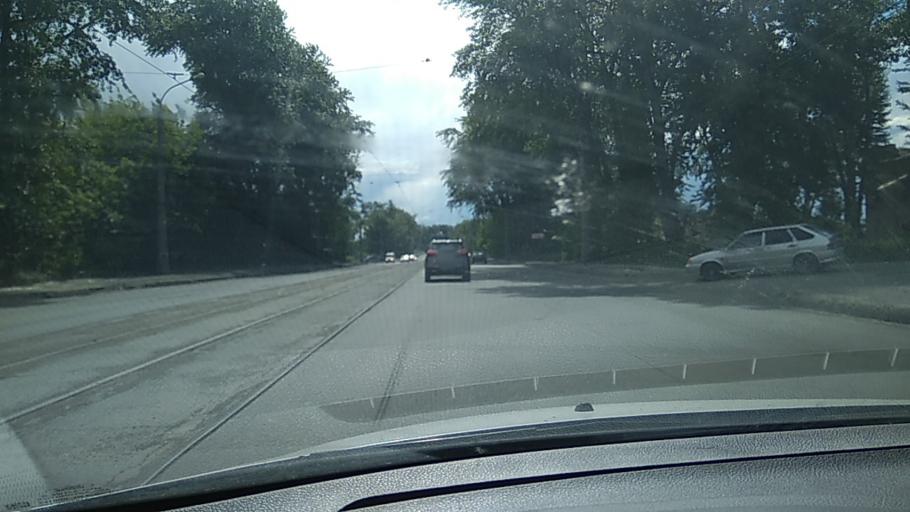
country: RU
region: Sverdlovsk
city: Nizhniy Tagil
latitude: 57.9258
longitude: 59.9914
